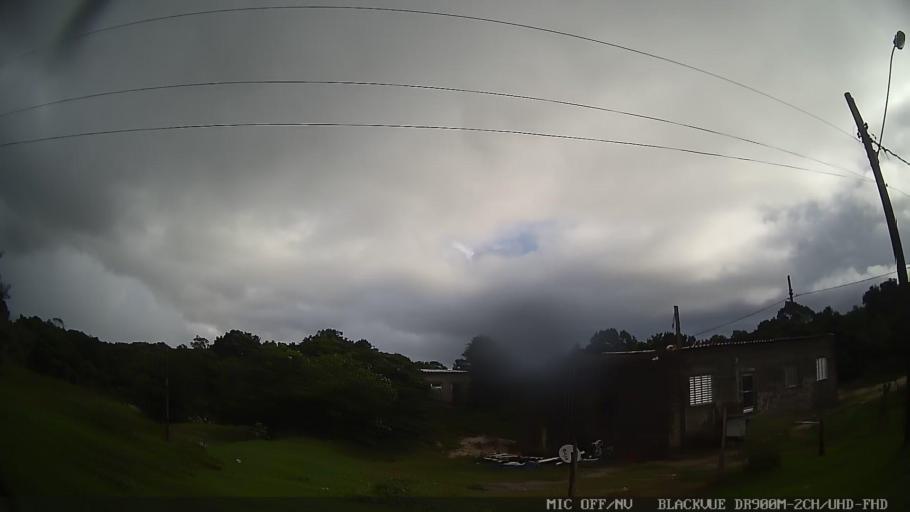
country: BR
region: Sao Paulo
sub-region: Peruibe
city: Peruibe
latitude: -24.2476
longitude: -46.9017
